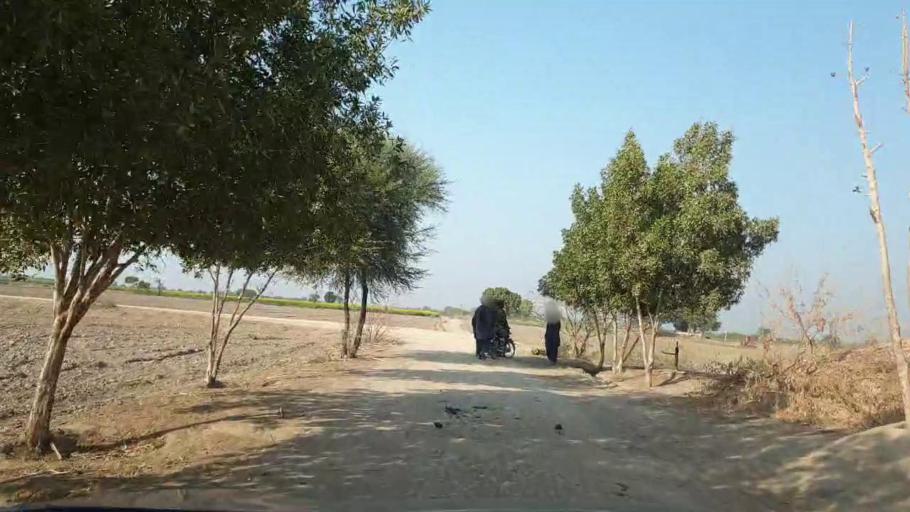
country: PK
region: Sindh
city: Tando Allahyar
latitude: 25.5159
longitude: 68.8421
